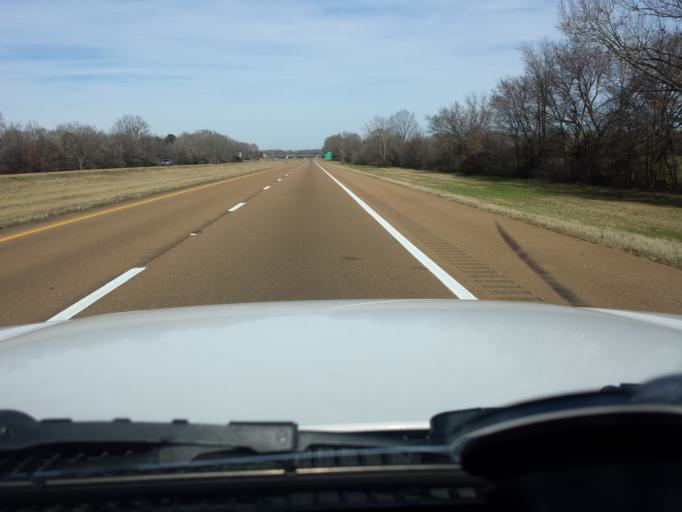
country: US
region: Mississippi
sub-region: Madison County
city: Canton
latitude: 32.6581
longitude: -90.0616
